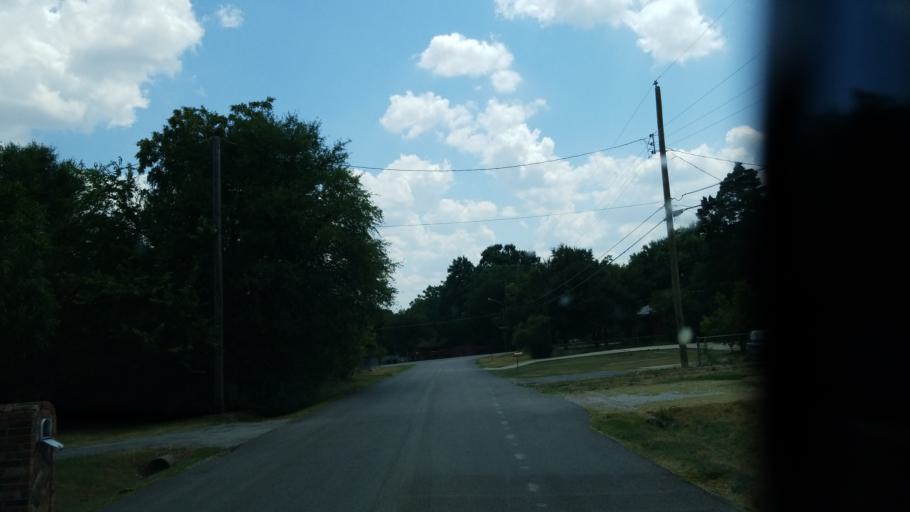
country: US
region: Texas
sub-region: Dallas County
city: Duncanville
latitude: 32.6735
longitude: -96.8892
